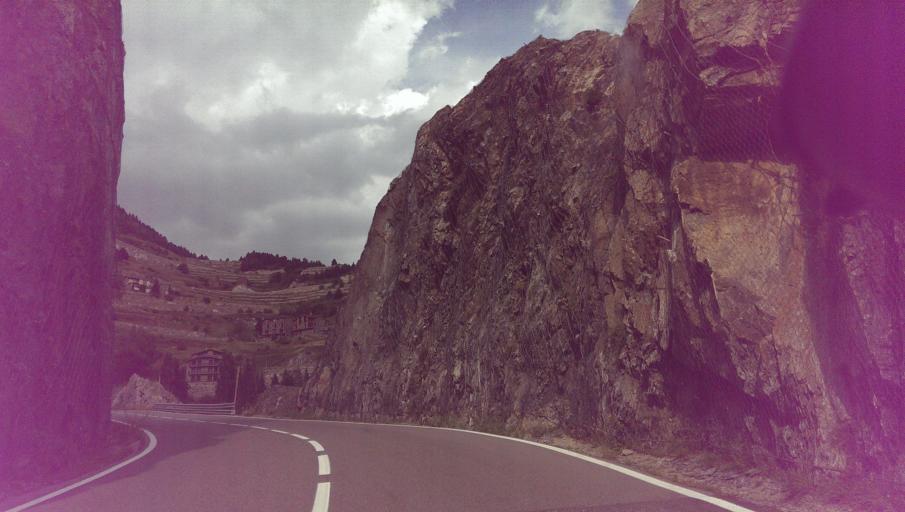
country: AD
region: Canillo
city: Canillo
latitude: 42.5678
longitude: 1.5963
